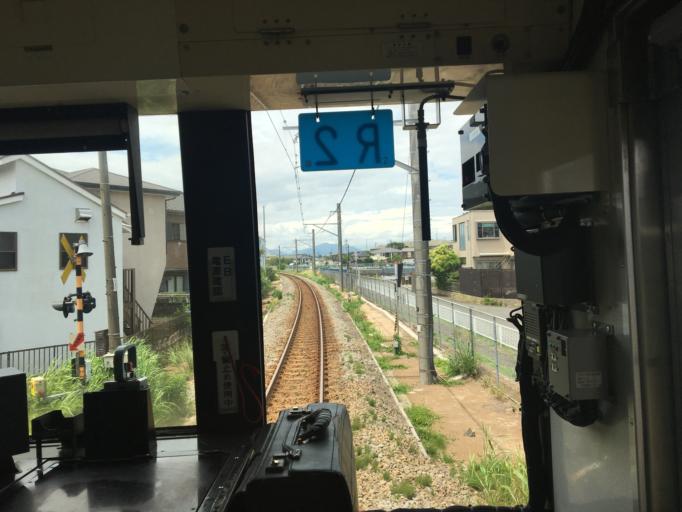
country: JP
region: Kanagawa
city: Chigasaki
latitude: 35.3597
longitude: 139.3984
